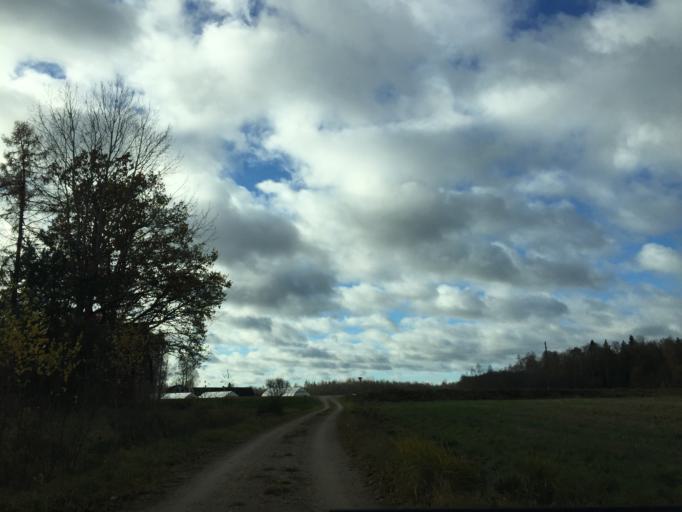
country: LV
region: Engure
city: Smarde
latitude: 56.9628
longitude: 23.2553
